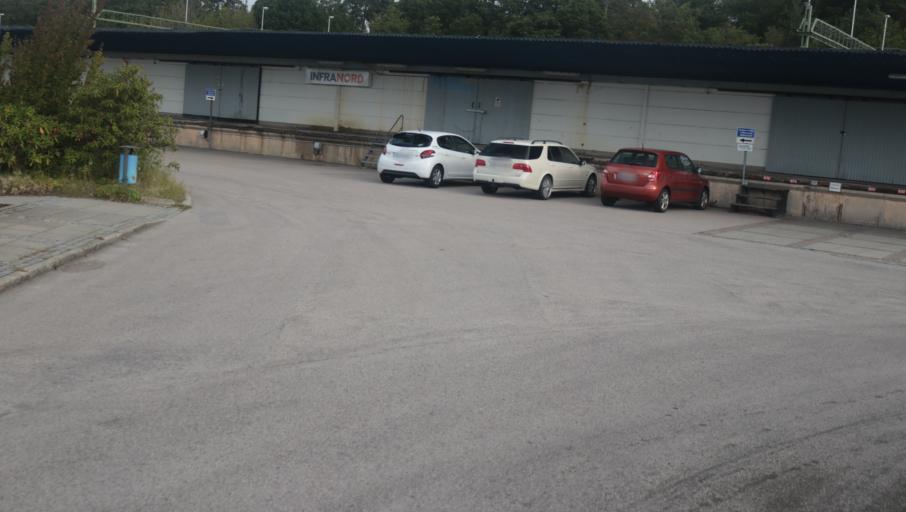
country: SE
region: Blekinge
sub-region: Karlshamns Kommun
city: Karlshamn
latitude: 56.1761
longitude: 14.8671
